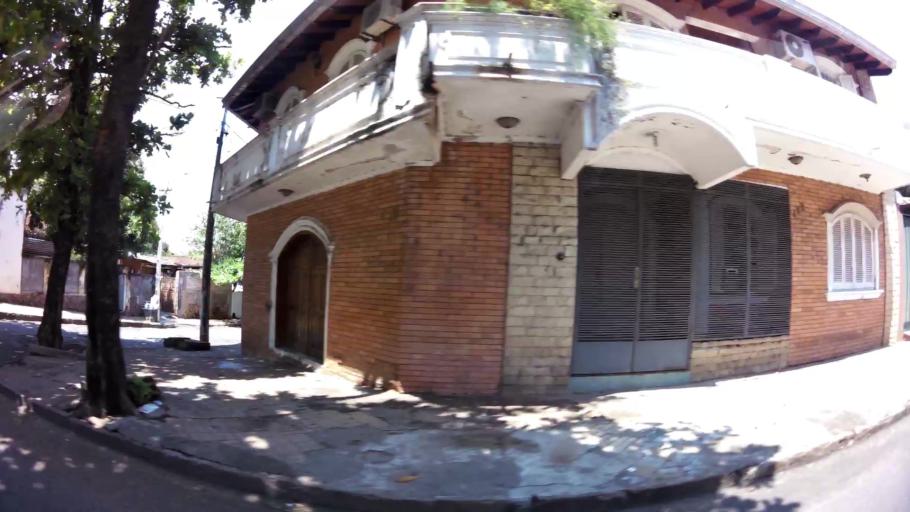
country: PY
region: Asuncion
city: Asuncion
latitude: -25.2999
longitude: -57.6412
